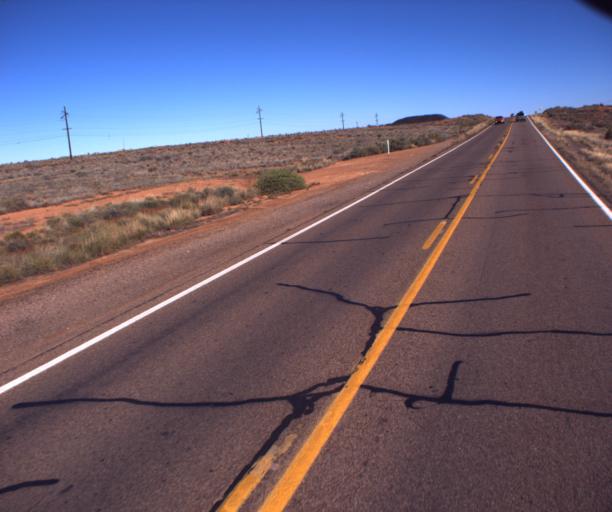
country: US
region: Arizona
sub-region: Navajo County
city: Holbrook
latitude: 34.8807
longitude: -110.1626
